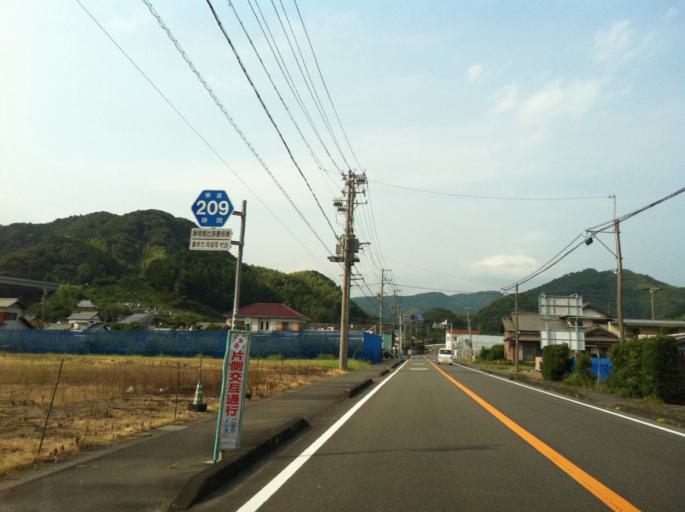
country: JP
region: Shizuoka
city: Fujieda
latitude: 34.9165
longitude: 138.2689
